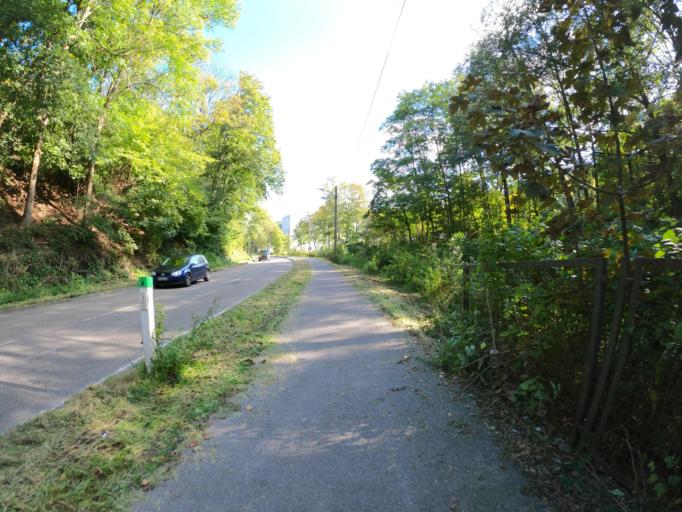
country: DE
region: North Rhine-Westphalia
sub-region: Regierungsbezirk Arnsberg
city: Schwelm
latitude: 51.2560
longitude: 7.2355
